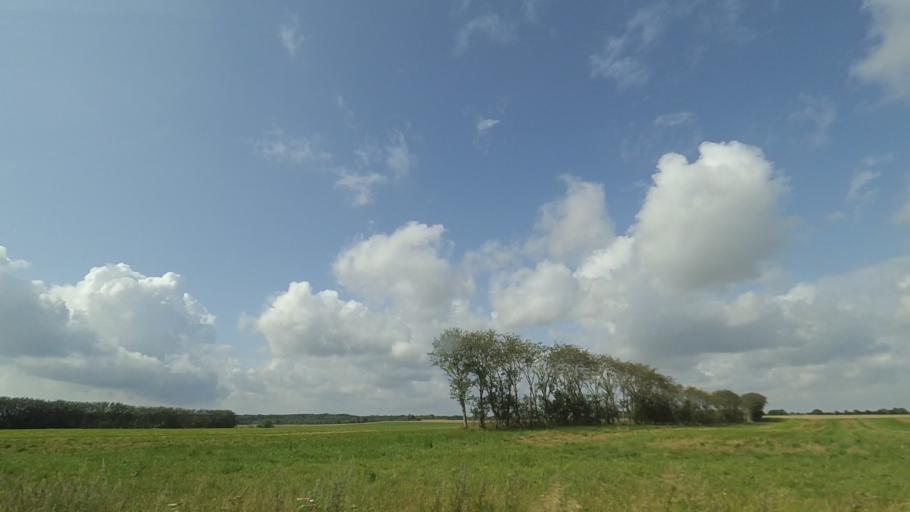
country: DK
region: Central Jutland
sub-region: Syddjurs Kommune
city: Ryomgard
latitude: 56.4729
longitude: 10.5088
